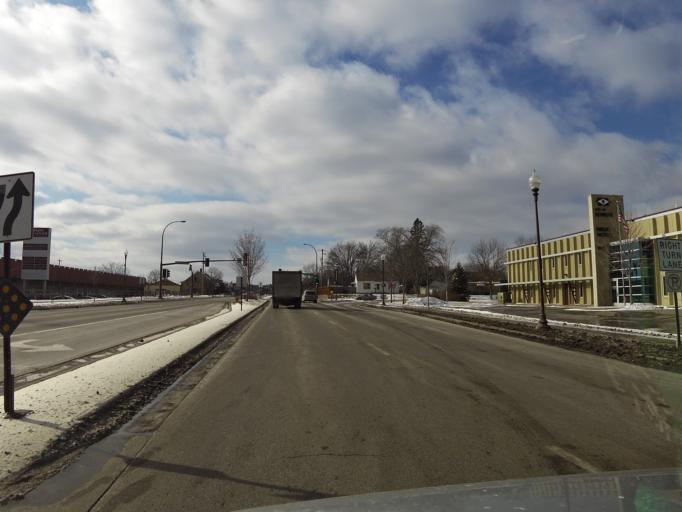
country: US
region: Minnesota
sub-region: Hennepin County
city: Minnetonka Mills
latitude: 44.9209
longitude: -93.4207
